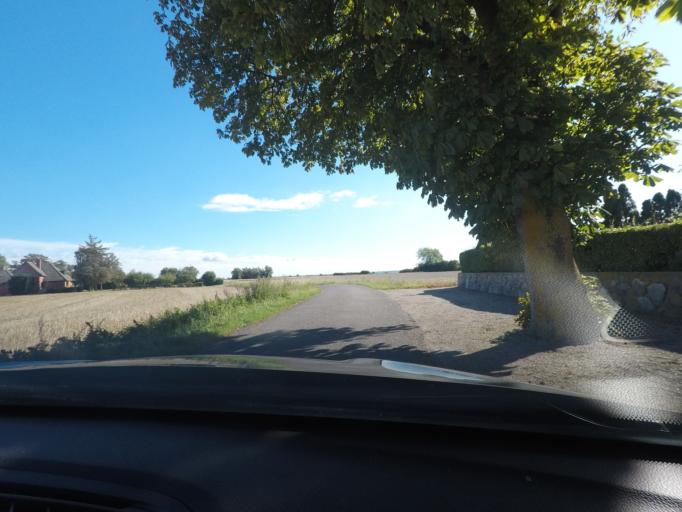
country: DK
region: Zealand
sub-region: Lolland Kommune
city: Maribo
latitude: 54.9724
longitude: 11.5232
